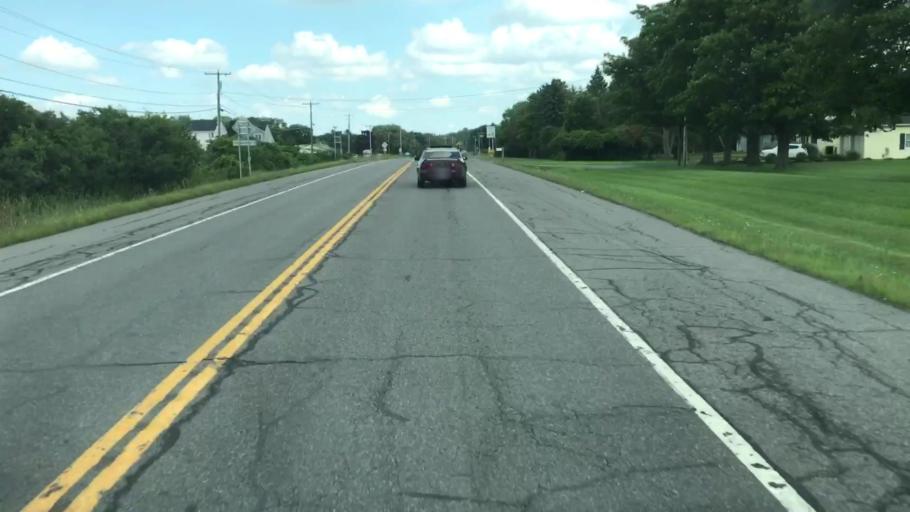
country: US
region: New York
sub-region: Onondaga County
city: Westvale
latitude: 42.9969
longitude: -76.2073
